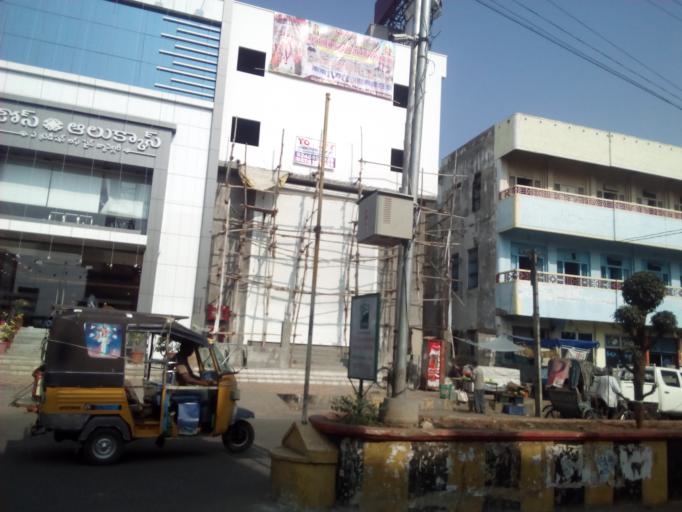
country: IN
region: Andhra Pradesh
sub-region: East Godavari
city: Rajahmundry
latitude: 16.9962
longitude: 81.7739
